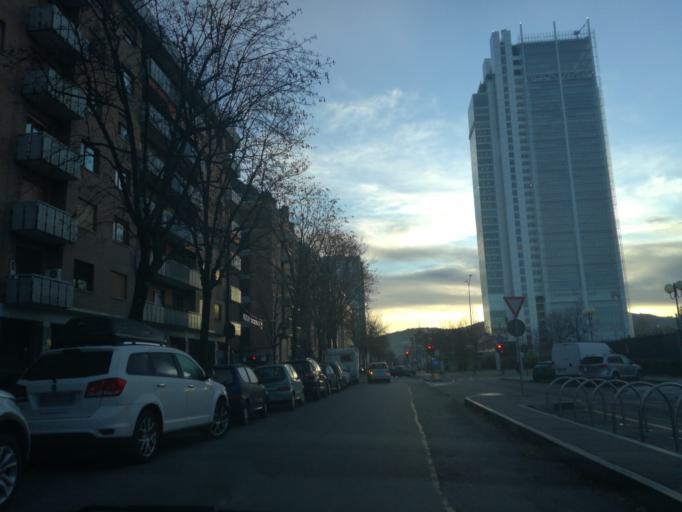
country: IT
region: Piedmont
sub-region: Provincia di Torino
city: Turin
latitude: 45.0712
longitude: 7.6598
